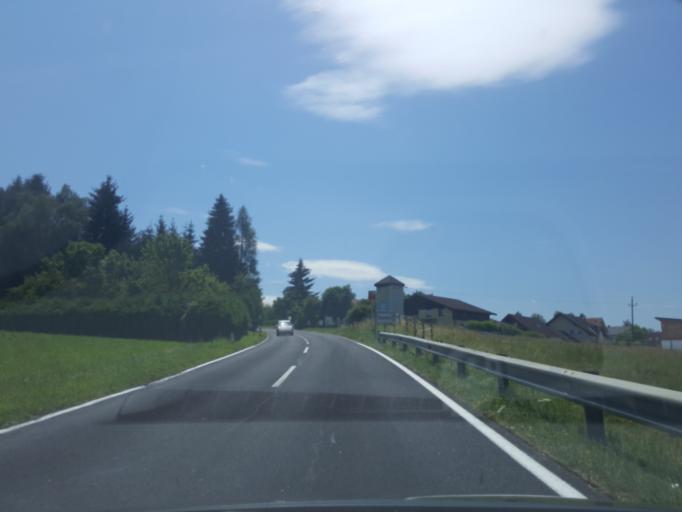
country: AT
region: Upper Austria
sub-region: Politischer Bezirk Vocklabruck
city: Seewalchen
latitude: 47.9641
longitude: 13.5716
